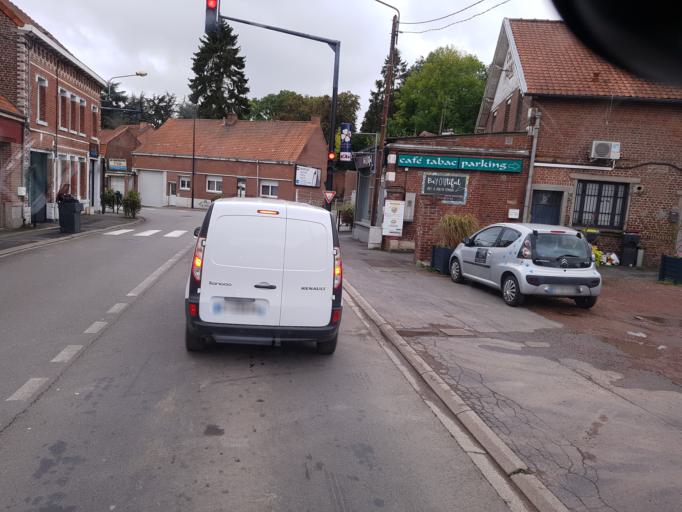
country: FR
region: Nord-Pas-de-Calais
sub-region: Departement du Pas-de-Calais
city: Souchez
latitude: 50.3937
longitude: 2.7429
